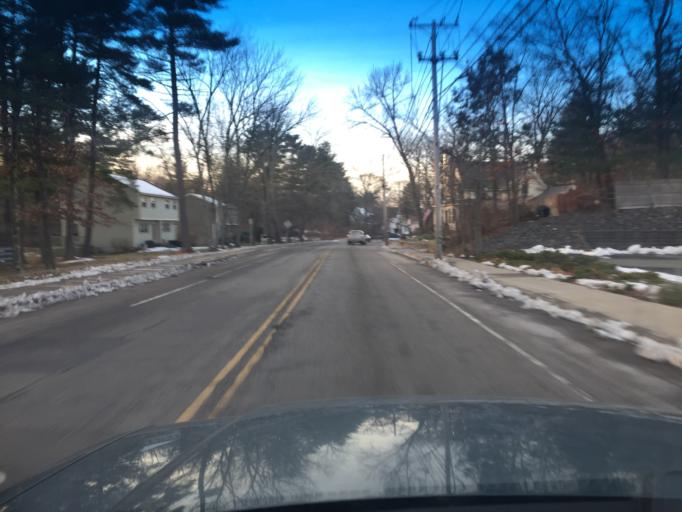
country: US
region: Massachusetts
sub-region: Norfolk County
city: Franklin
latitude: 42.0852
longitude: -71.4078
